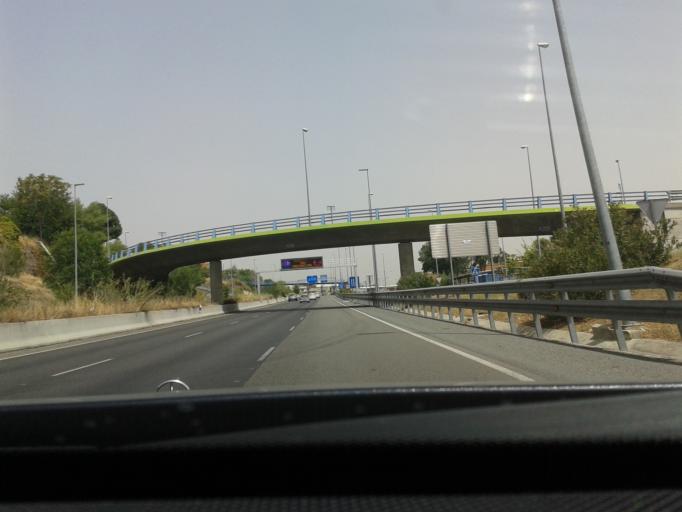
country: ES
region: Madrid
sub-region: Provincia de Madrid
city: Barajas de Madrid
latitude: 40.4701
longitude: -3.5749
